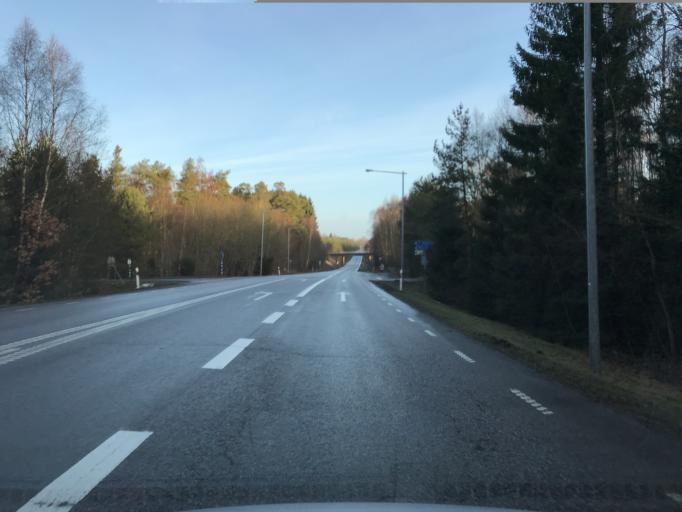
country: SE
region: Skane
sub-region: Hassleholms Kommun
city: Bjarnum
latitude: 56.2347
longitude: 13.7136
